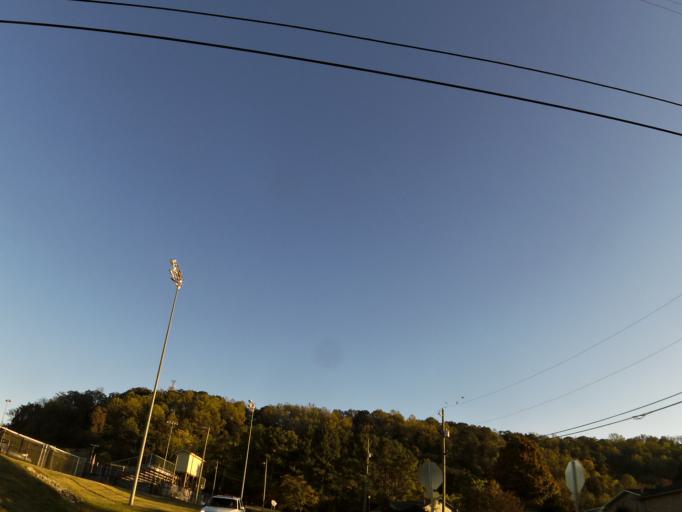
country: US
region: Tennessee
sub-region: Knox County
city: Farragut
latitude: 35.9868
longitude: -84.0801
